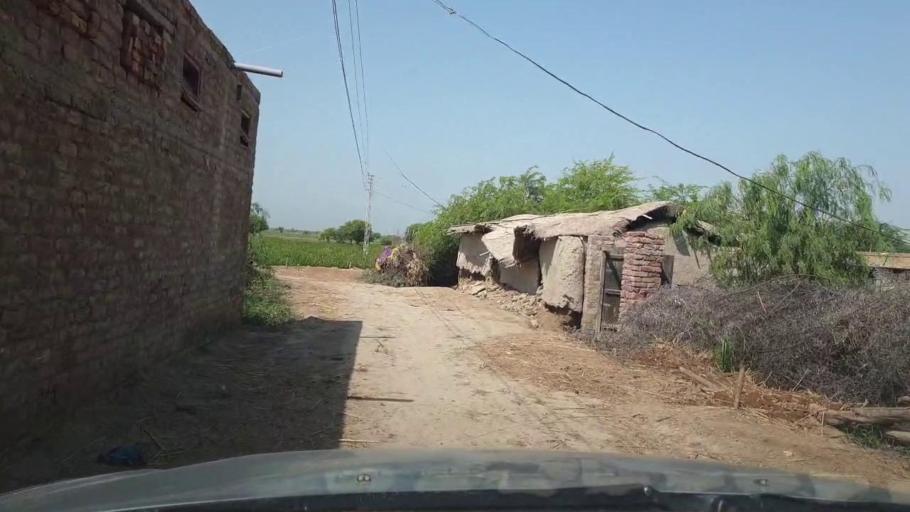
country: PK
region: Sindh
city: Chambar
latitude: 25.1979
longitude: 68.7757
